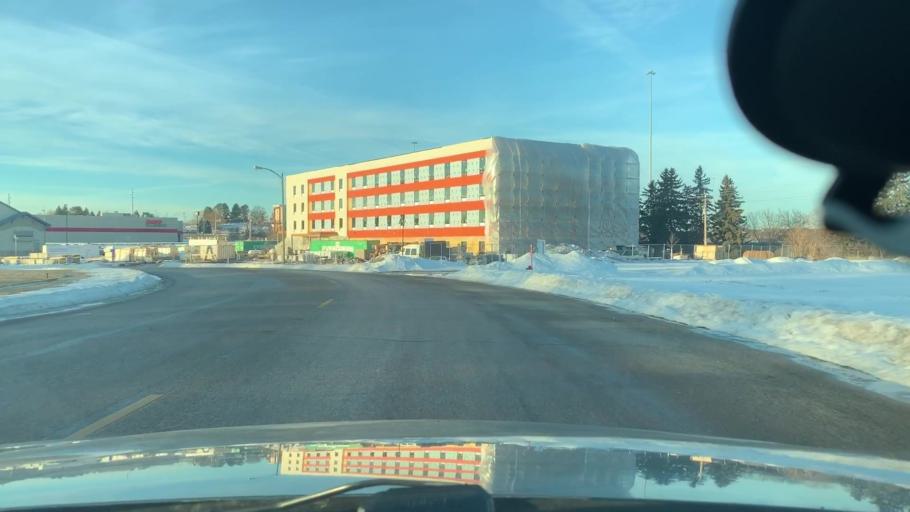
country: US
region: North Dakota
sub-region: Burleigh County
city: Bismarck
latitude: 46.8284
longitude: -100.8103
